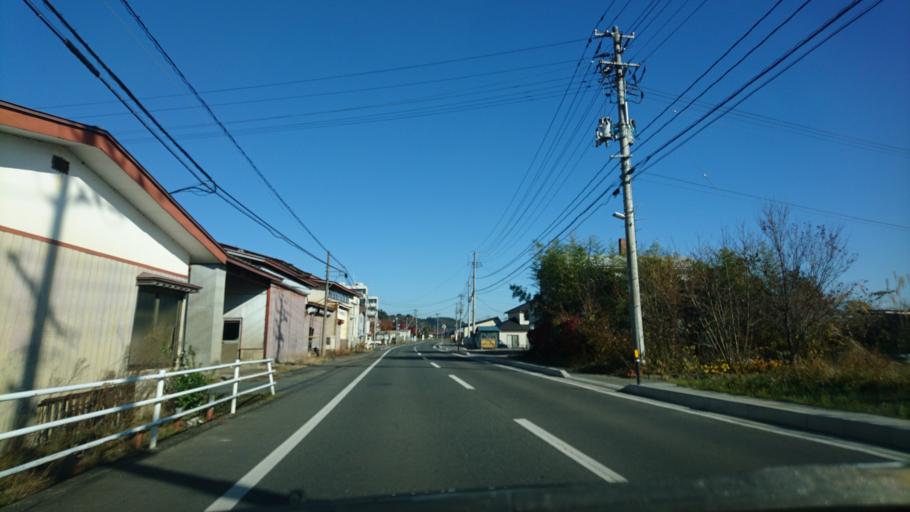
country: JP
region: Iwate
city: Mizusawa
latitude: 39.0622
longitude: 141.1253
